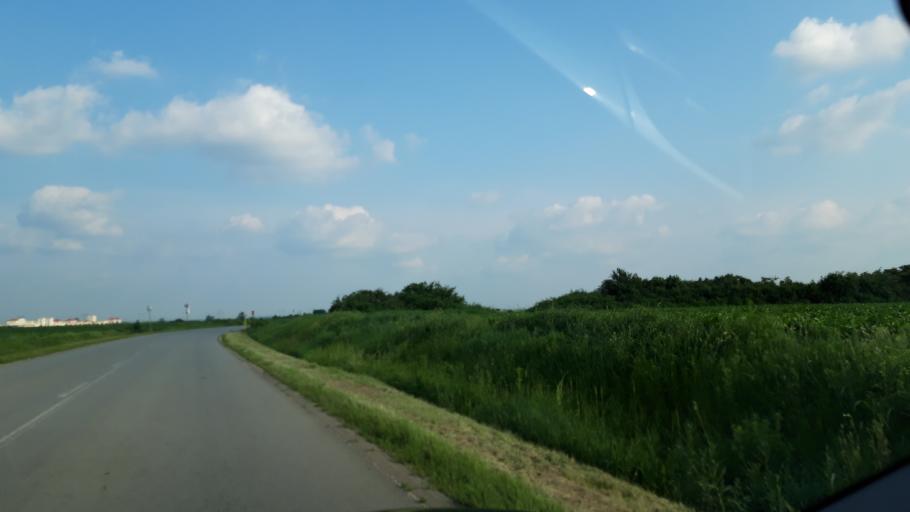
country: RS
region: Autonomna Pokrajina Vojvodina
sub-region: Sremski Okrug
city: Ingija
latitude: 45.0769
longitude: 20.1230
